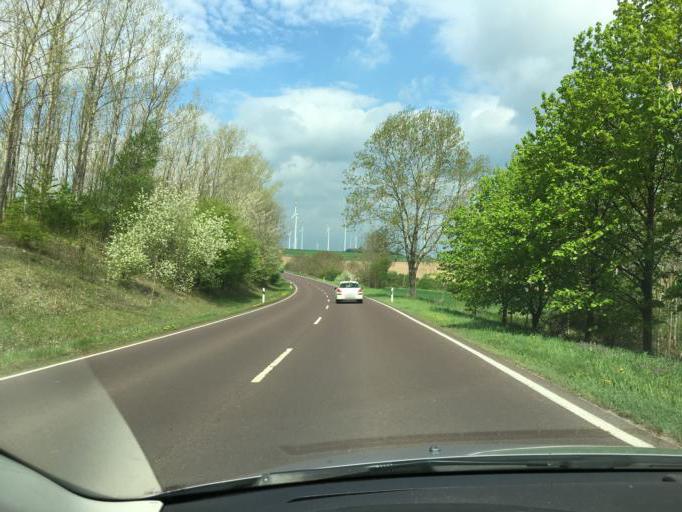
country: DE
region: Saxony-Anhalt
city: Alsleben
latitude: 51.7078
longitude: 11.6632
